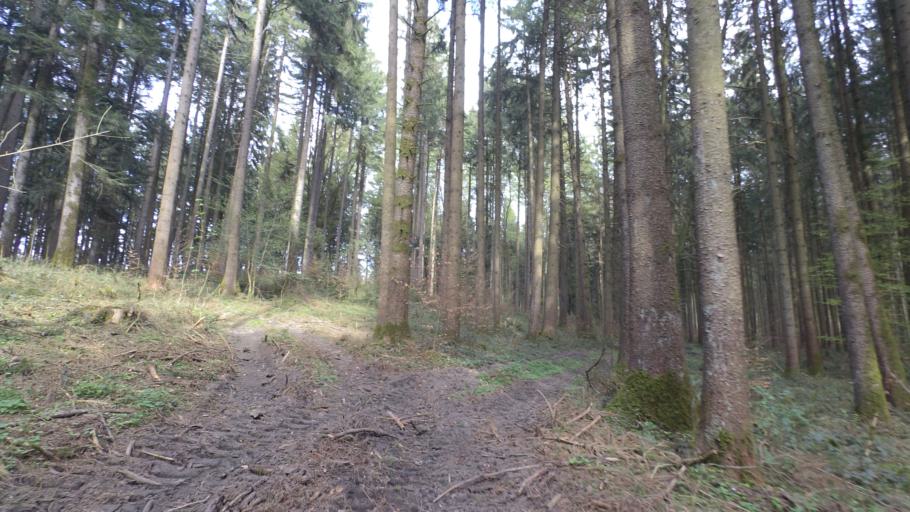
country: DE
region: Bavaria
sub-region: Upper Bavaria
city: Nussdorf
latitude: 47.9162
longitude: 12.5756
